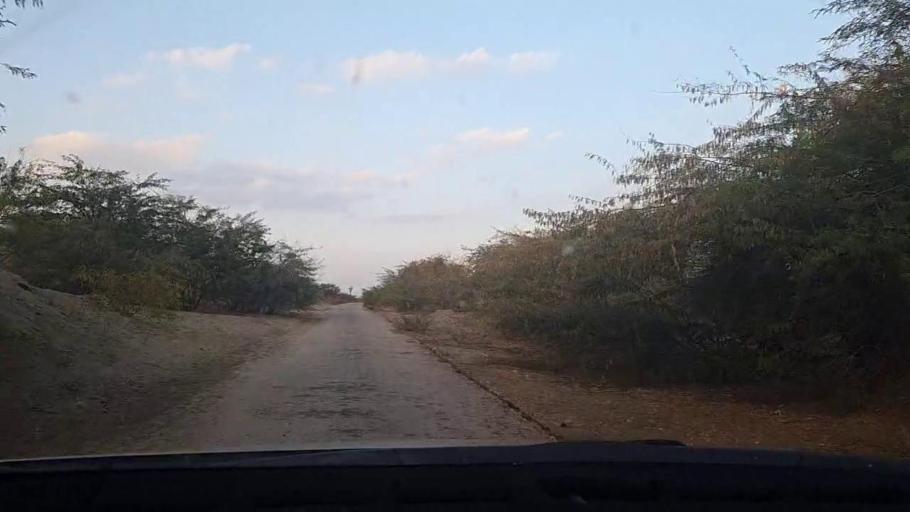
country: PK
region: Sindh
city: Tando Mittha Khan
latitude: 25.9451
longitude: 69.3421
